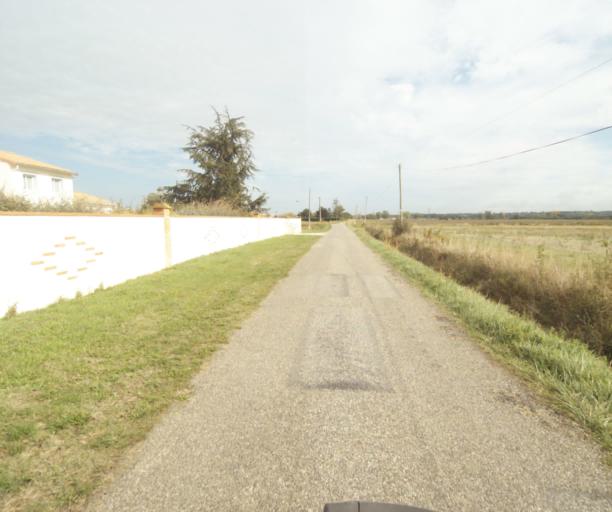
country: FR
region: Midi-Pyrenees
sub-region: Departement du Tarn-et-Garonne
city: Finhan
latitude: 43.9026
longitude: 1.2363
